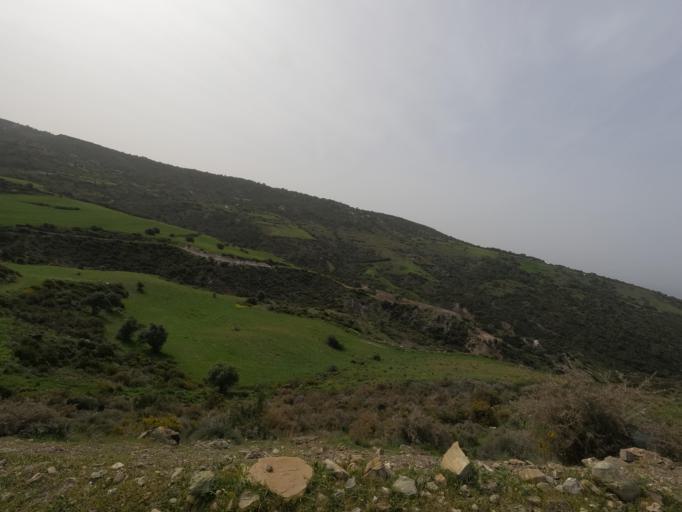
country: CY
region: Pafos
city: Pegeia
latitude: 34.9495
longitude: 32.3530
